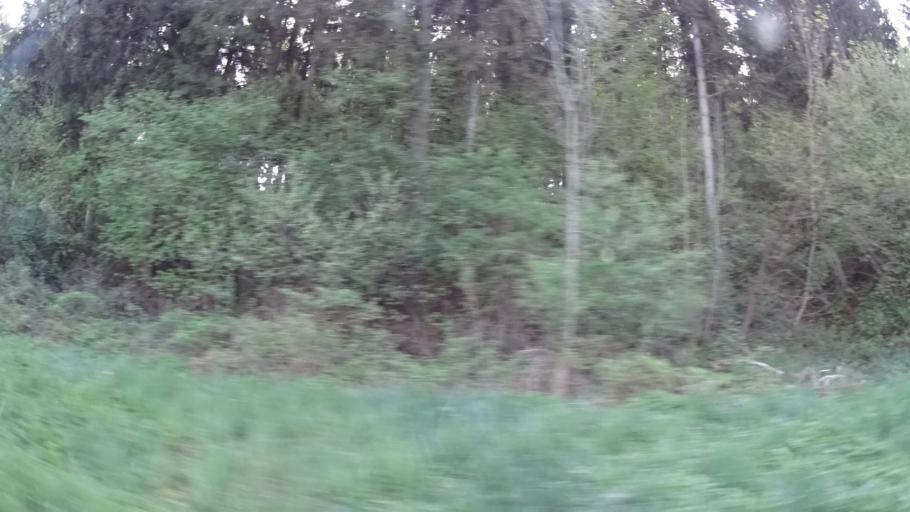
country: DE
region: Baden-Wuerttemberg
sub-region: Tuebingen Region
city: Haigerloch
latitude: 48.3891
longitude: 8.7899
